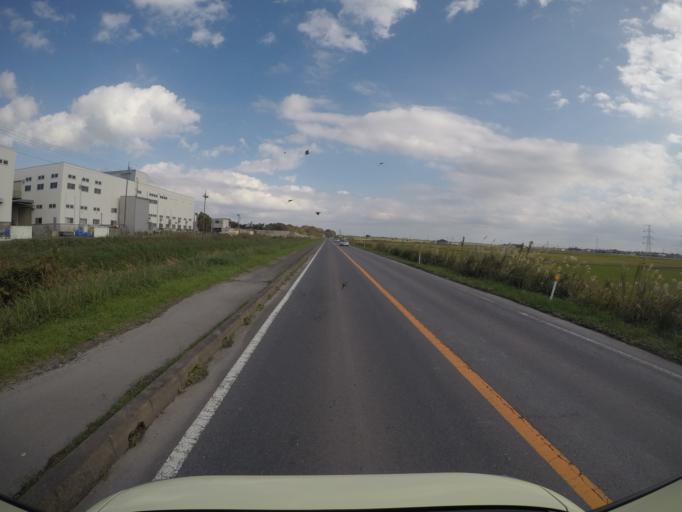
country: JP
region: Ibaraki
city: Iwai
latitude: 35.9912
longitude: 139.9031
